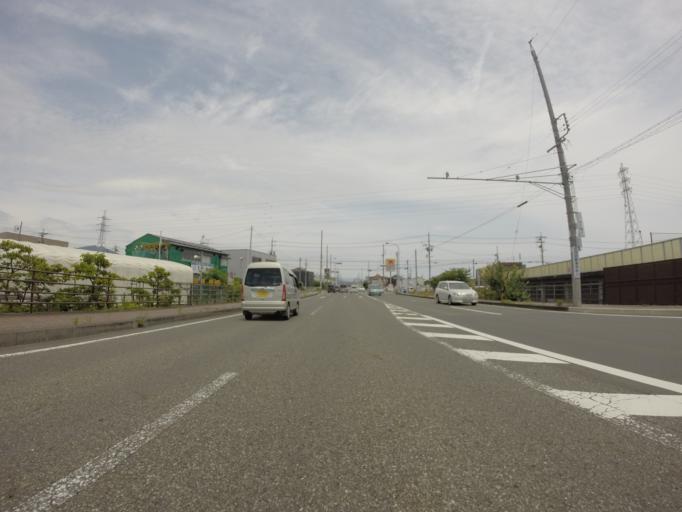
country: JP
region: Shizuoka
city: Shizuoka-shi
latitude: 35.0031
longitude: 138.4221
